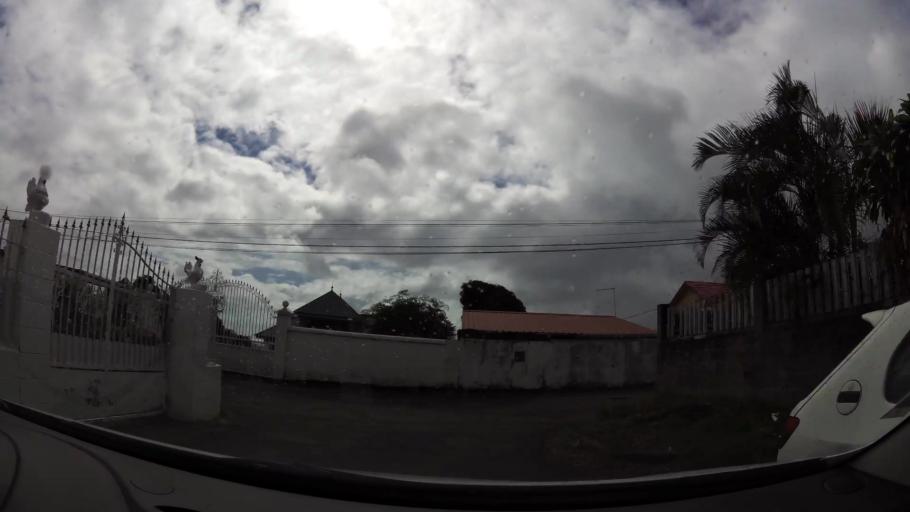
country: RE
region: Reunion
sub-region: Reunion
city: Sainte-Marie
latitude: -20.9016
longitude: 55.5568
